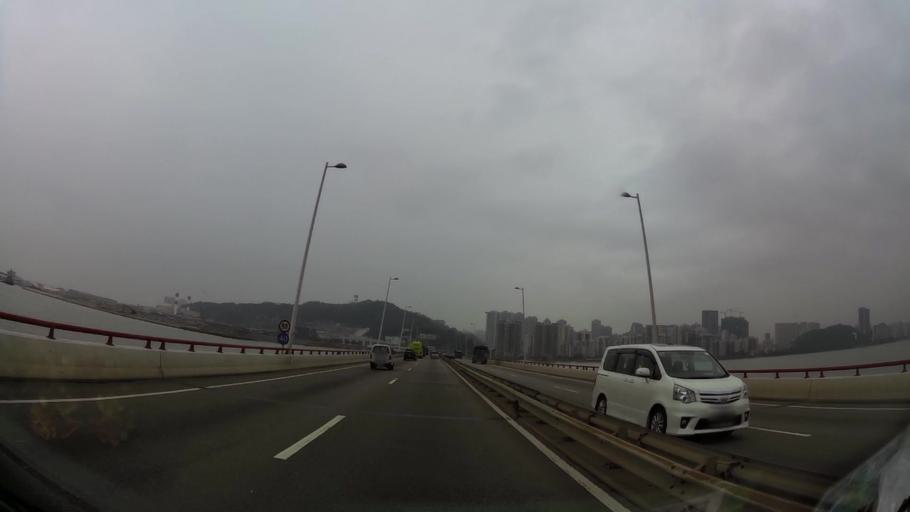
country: MO
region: Macau
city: Macau
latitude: 22.1728
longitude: 113.5635
